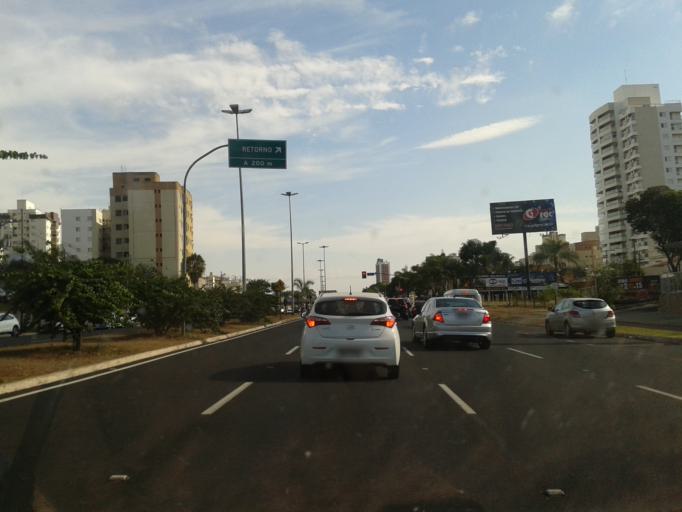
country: BR
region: Minas Gerais
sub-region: Uberlandia
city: Uberlandia
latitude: -18.9167
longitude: -48.2647
